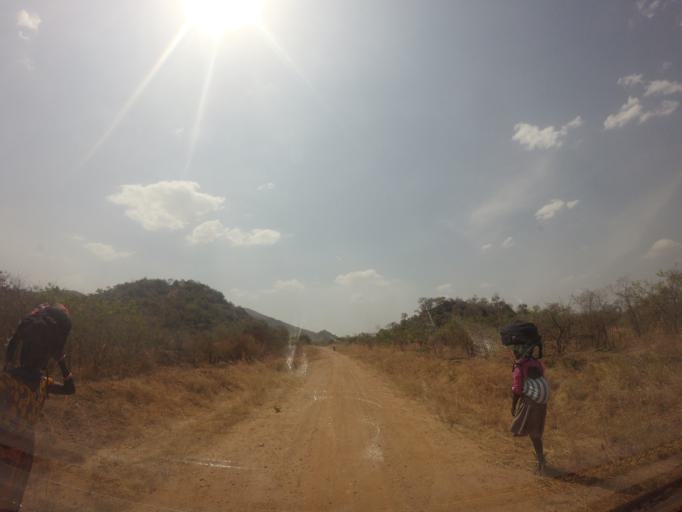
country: UG
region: Northern Region
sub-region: Arua District
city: Arua
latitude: 2.8973
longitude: 31.1073
